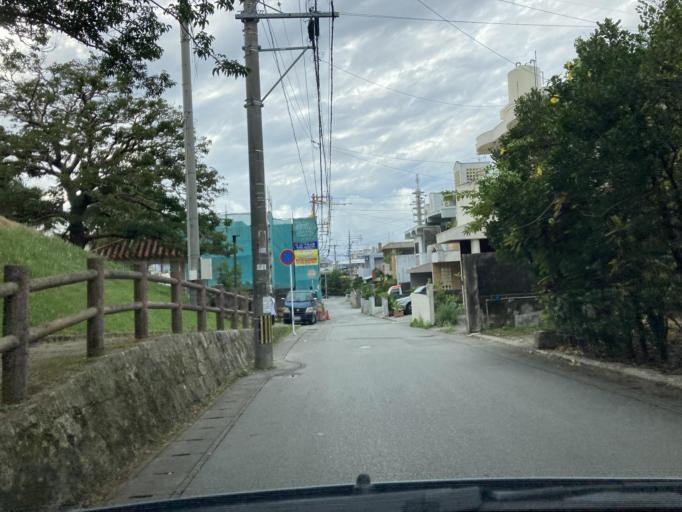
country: JP
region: Okinawa
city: Naha-shi
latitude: 26.2193
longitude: 127.7311
